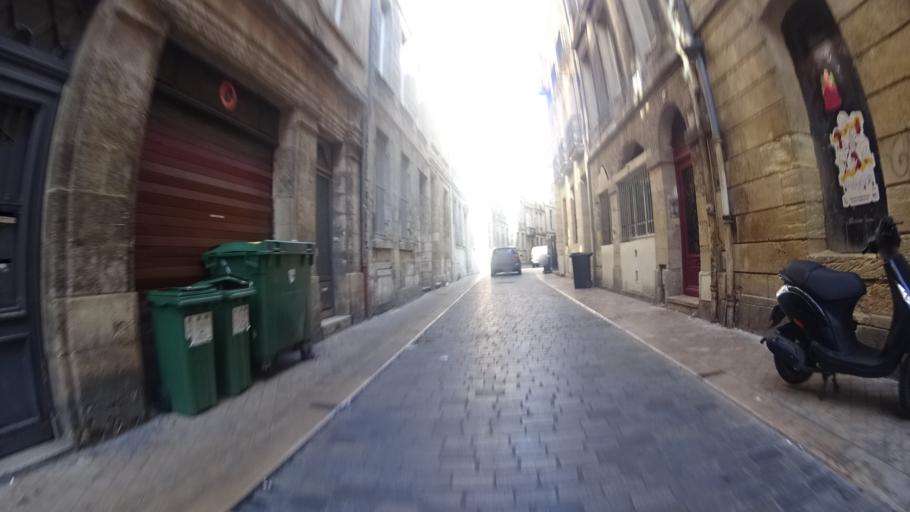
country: FR
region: Aquitaine
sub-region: Departement de la Gironde
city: Bordeaux
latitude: 44.8398
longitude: -0.5718
